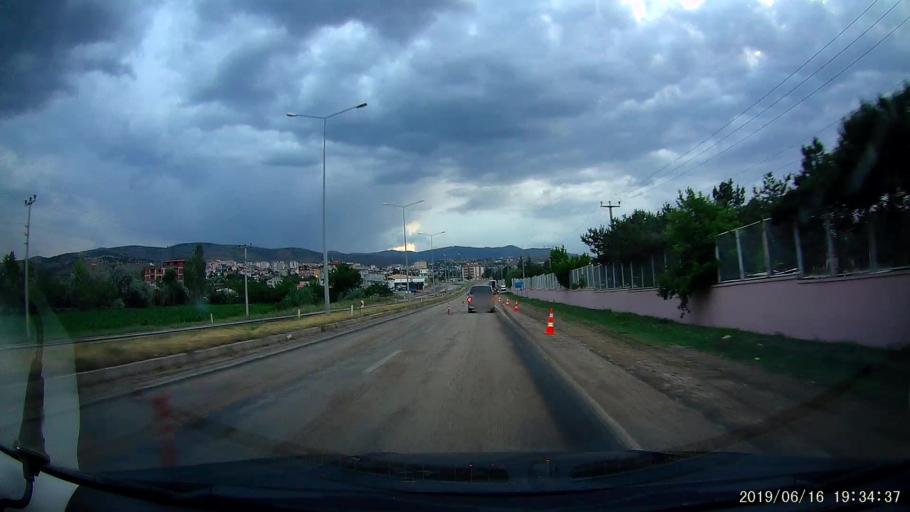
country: TR
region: Sivas
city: Susehri
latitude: 40.1697
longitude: 38.1037
